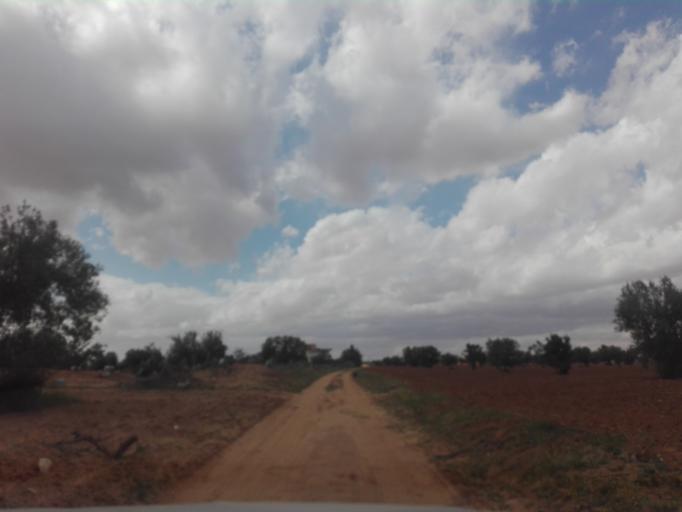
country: TN
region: Safaqis
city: Sfax
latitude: 34.6940
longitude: 10.4475
